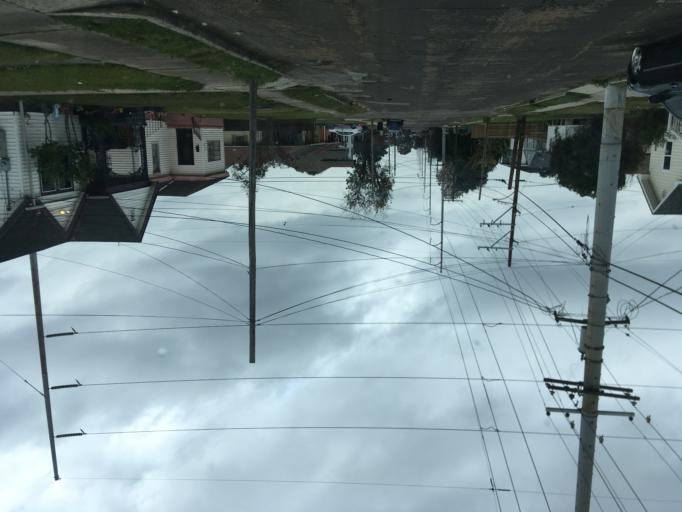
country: US
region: Louisiana
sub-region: Orleans Parish
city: New Orleans
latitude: 29.9924
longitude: -90.0600
